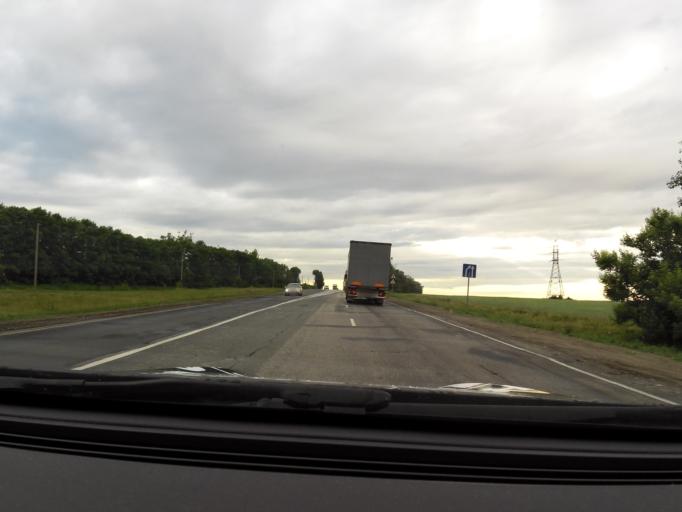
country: RU
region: Chuvashia
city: Tsivil'sk
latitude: 55.7953
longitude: 47.6603
